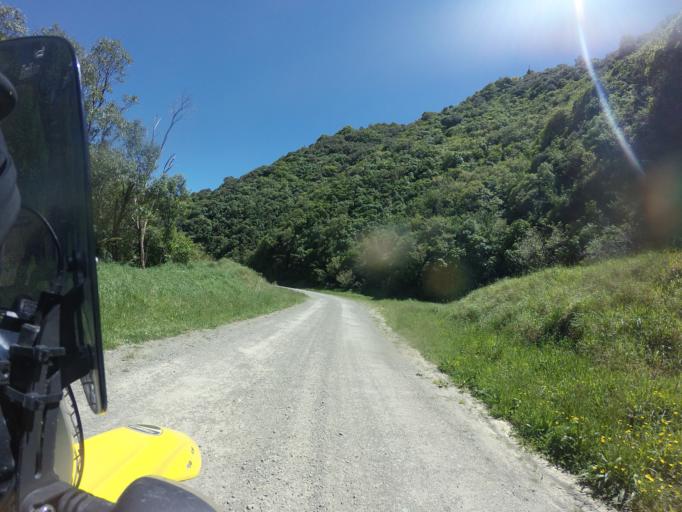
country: NZ
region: Bay of Plenty
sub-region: Opotiki District
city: Opotiki
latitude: -38.4168
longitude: 177.4006
